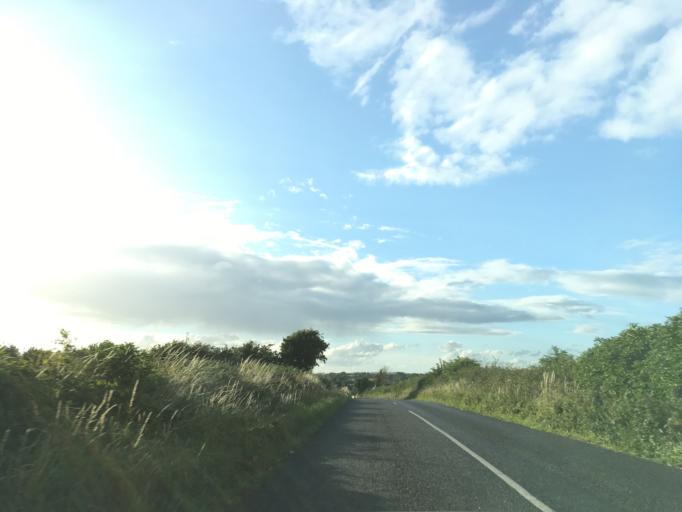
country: IE
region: Munster
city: Cashel
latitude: 52.4764
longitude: -7.9264
